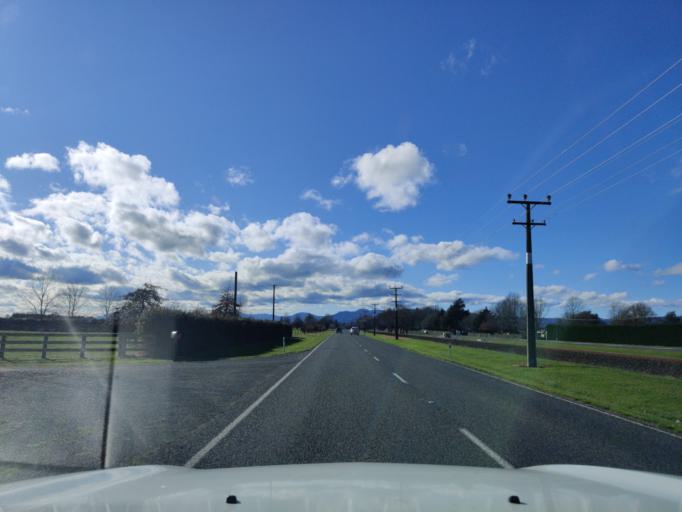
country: NZ
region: Waikato
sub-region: Matamata-Piako District
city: Matamata
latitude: -37.8349
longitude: 175.7658
